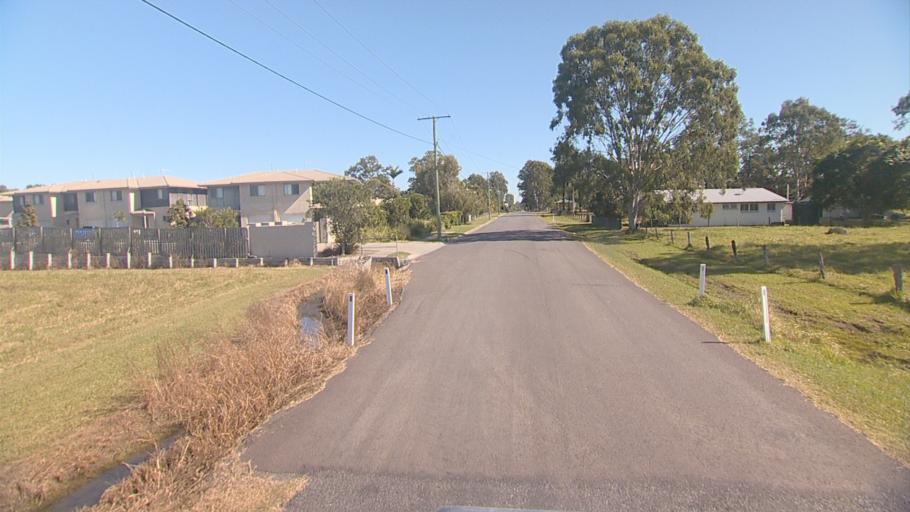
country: AU
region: Queensland
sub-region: Logan
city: Beenleigh
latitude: -27.6876
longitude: 153.2192
